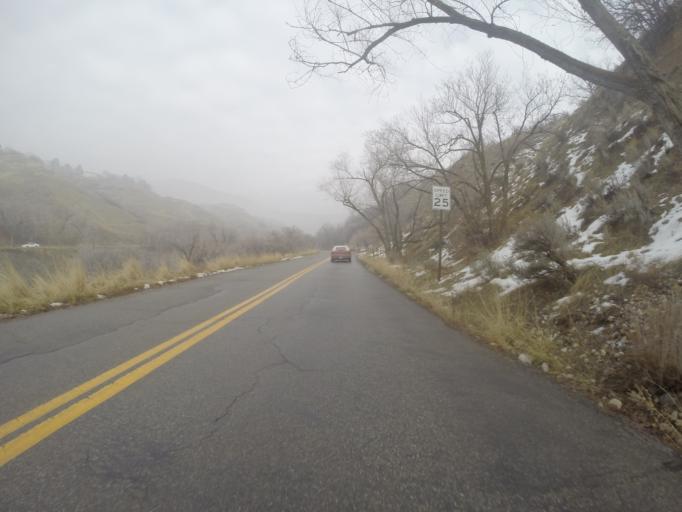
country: US
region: Utah
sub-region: Salt Lake County
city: Salt Lake City
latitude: 40.7870
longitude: -111.8812
